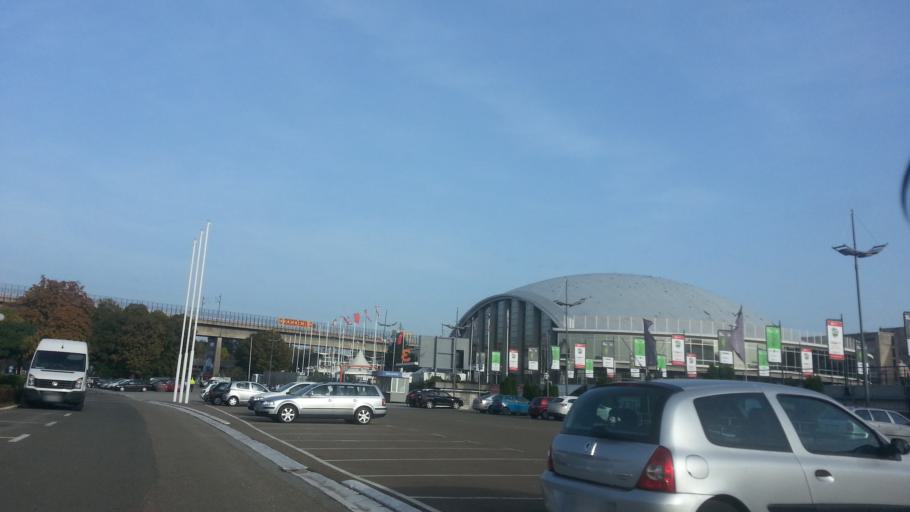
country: RS
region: Central Serbia
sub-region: Belgrade
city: Novi Beograd
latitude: 44.7968
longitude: 20.4370
